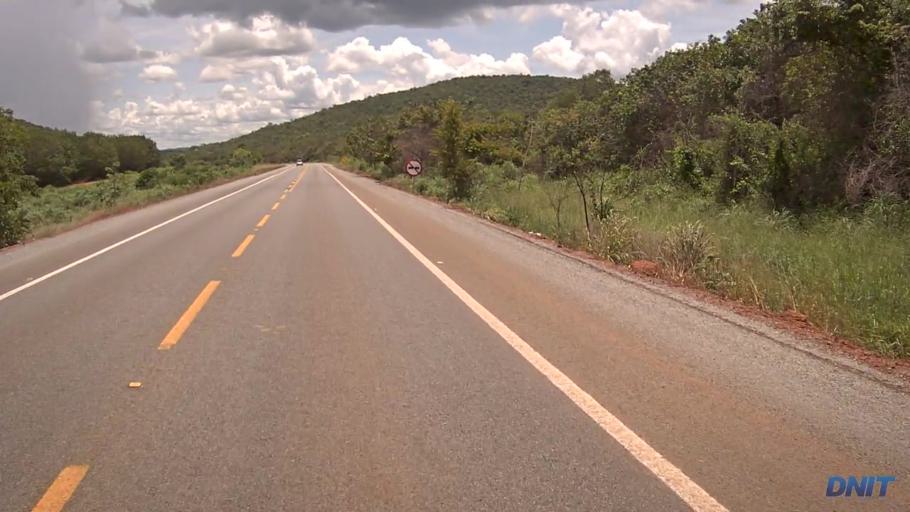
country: BR
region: Goias
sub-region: Barro Alto
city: Barro Alto
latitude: -14.9004
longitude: -48.9648
